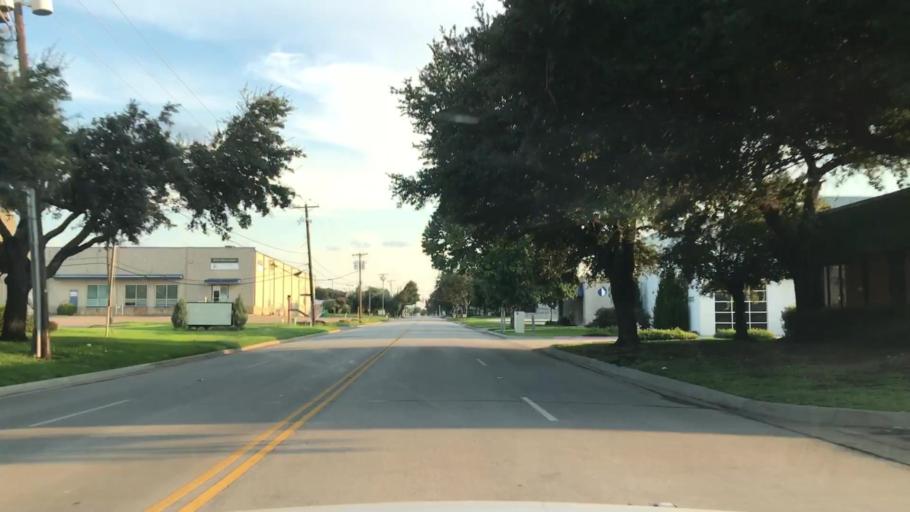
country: US
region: Texas
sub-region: Dallas County
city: Addison
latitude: 32.9364
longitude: -96.8305
